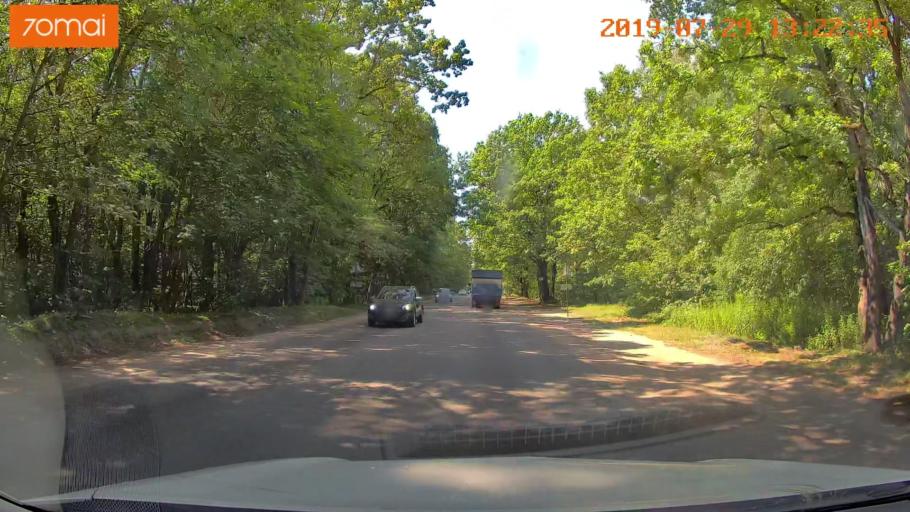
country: RU
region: Kaliningrad
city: Vzmorye
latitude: 54.7149
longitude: 20.3677
